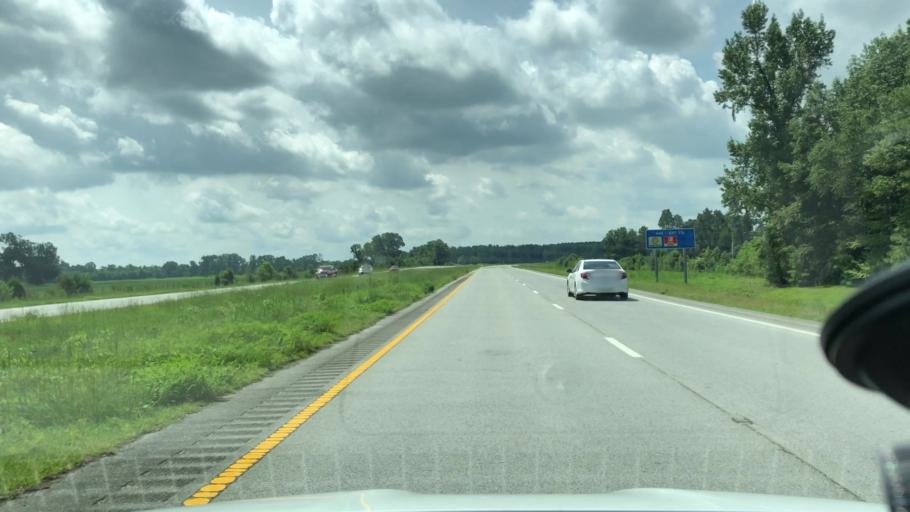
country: US
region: North Carolina
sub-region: Beaufort County
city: Washington
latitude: 35.5142
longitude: -77.0864
